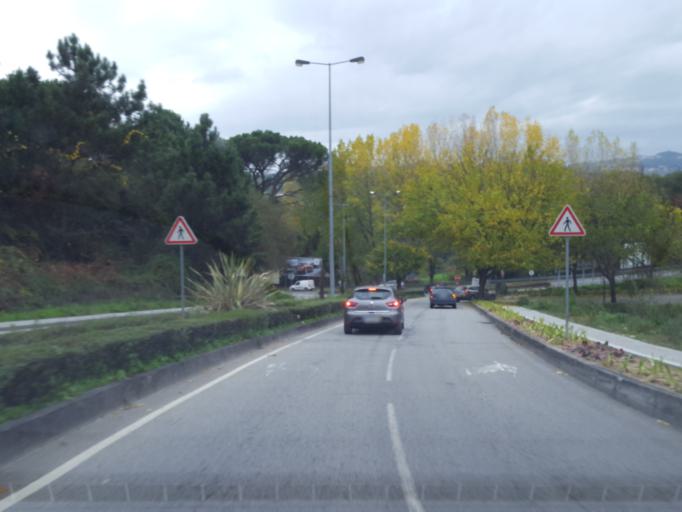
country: PT
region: Porto
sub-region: Marco de Canaveses
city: Marco de Canavezes
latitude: 41.1930
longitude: -8.1543
